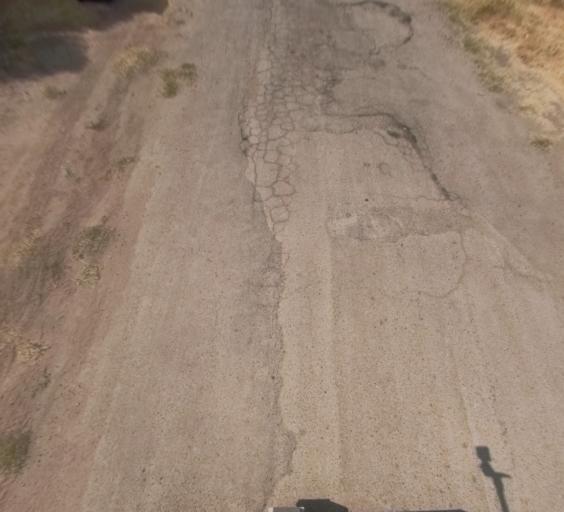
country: US
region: California
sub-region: Madera County
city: Fairmead
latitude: 37.0767
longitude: -120.1972
